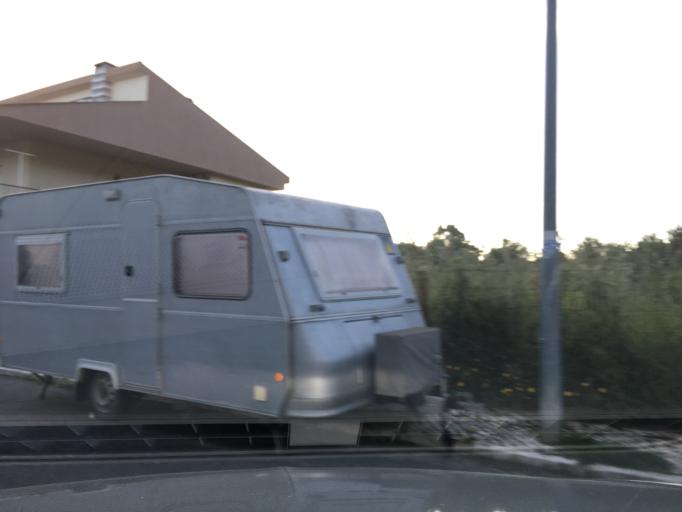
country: PT
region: Lisbon
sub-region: Oeiras
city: Barcarena
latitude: 38.7282
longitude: -9.2770
